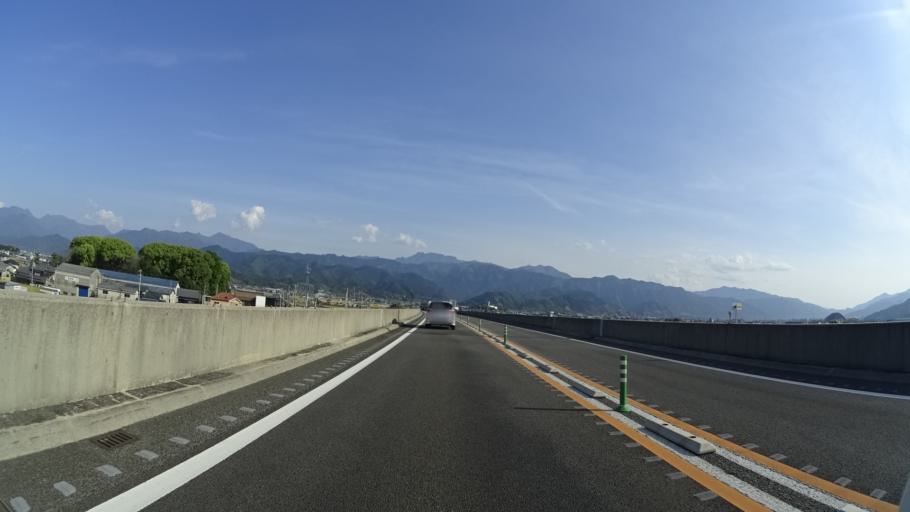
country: JP
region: Ehime
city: Saijo
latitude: 33.9119
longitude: 133.0732
